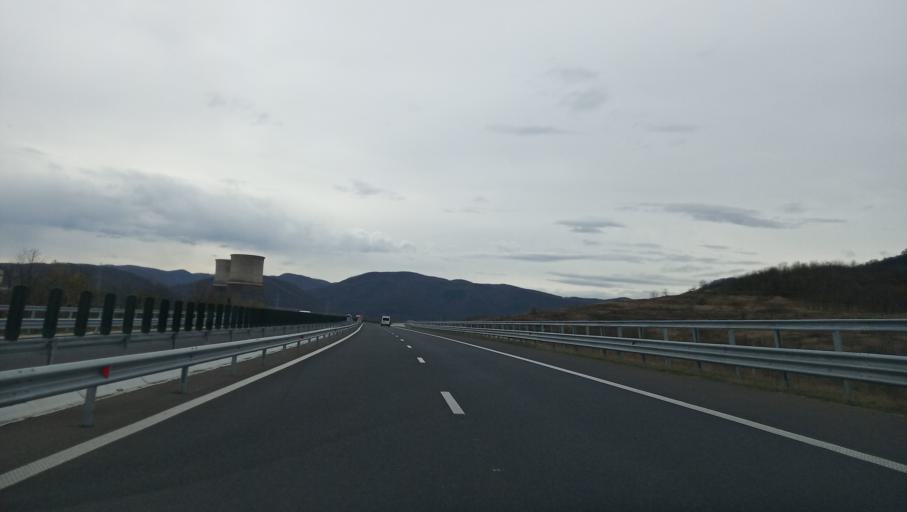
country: RO
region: Hunedoara
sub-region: Comuna Vetel
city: Vetel
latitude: 45.9241
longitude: 22.8287
